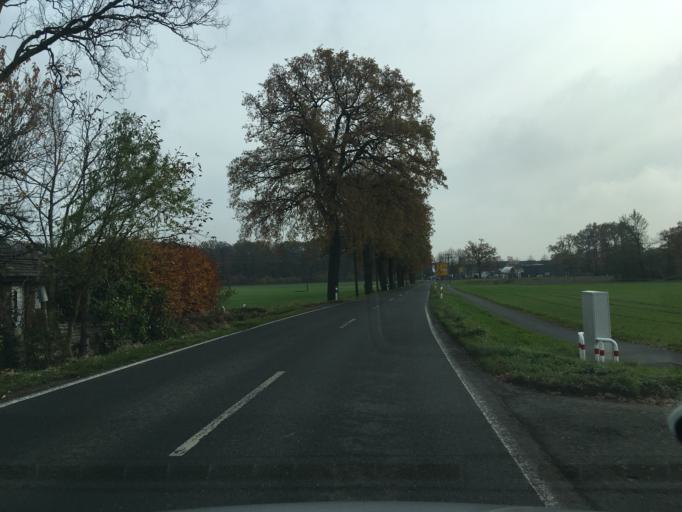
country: DE
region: North Rhine-Westphalia
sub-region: Regierungsbezirk Munster
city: Velen
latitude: 51.9029
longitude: 6.9747
